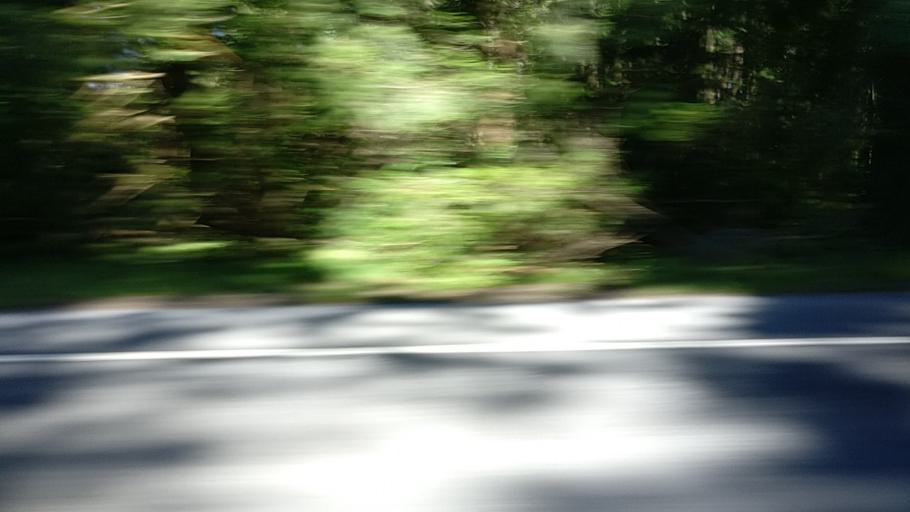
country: CA
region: British Columbia
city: Surrey
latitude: 49.0636
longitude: -122.8450
